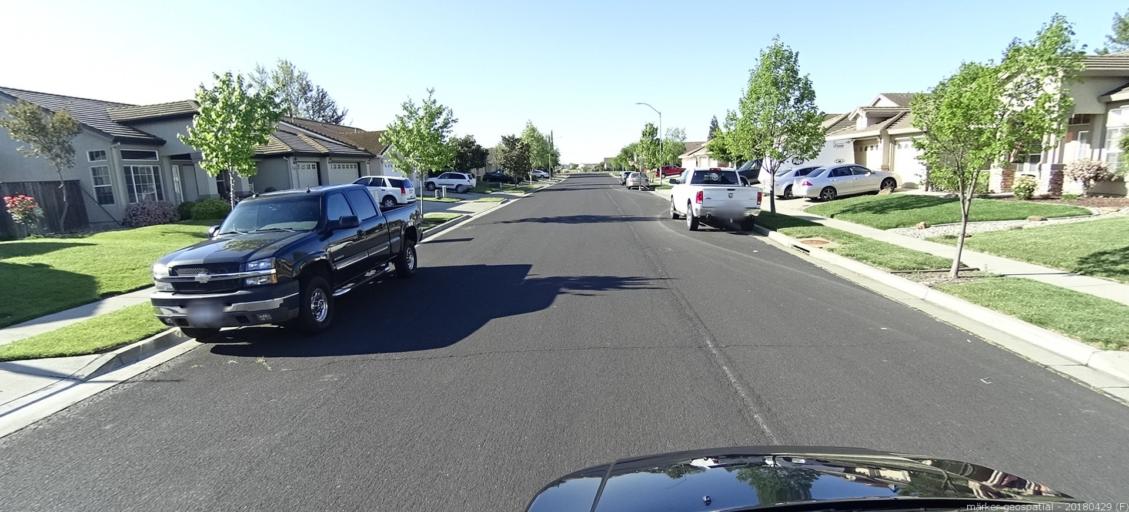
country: US
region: California
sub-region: Yolo County
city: West Sacramento
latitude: 38.5365
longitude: -121.5698
